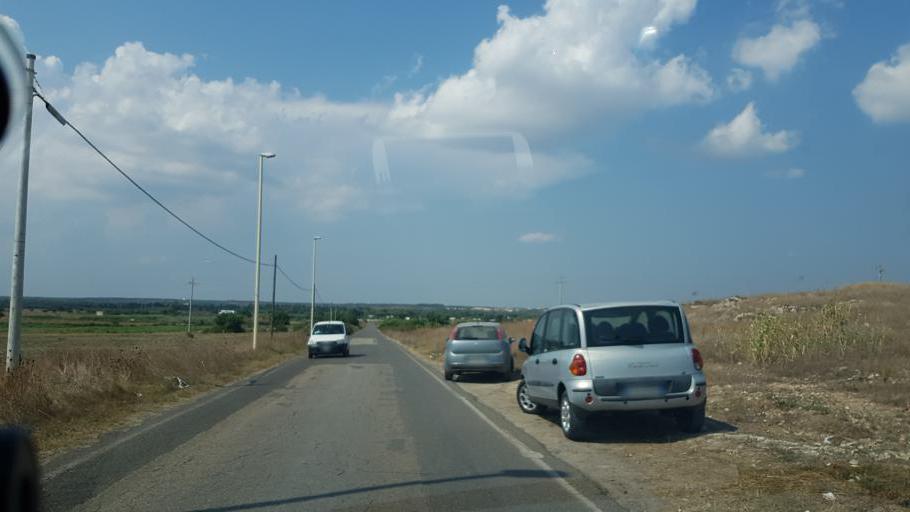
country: IT
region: Apulia
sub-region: Provincia di Taranto
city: Maruggio
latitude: 40.3049
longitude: 17.6346
